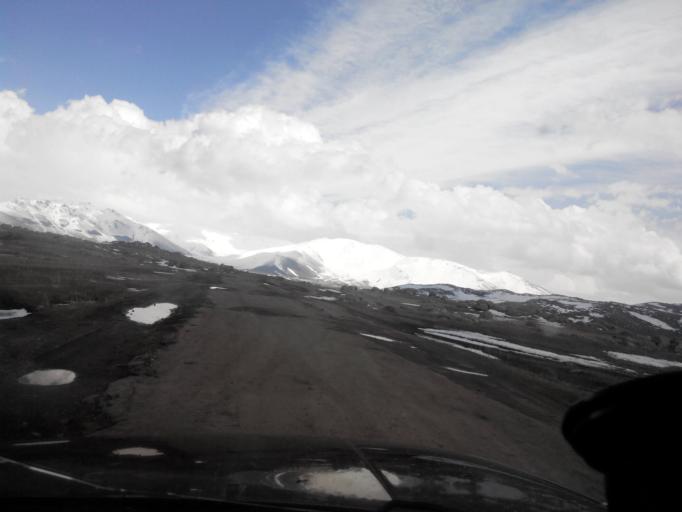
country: AM
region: Aragatsotn
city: Tsaghkahovit
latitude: 40.6441
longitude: 44.2787
